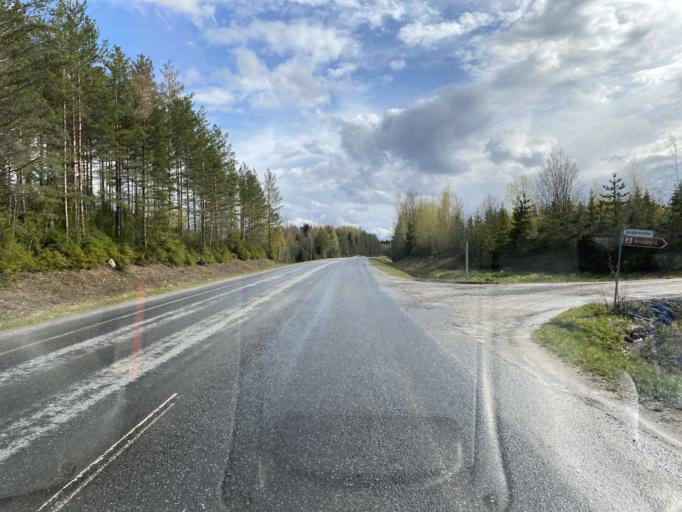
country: FI
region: Pirkanmaa
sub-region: Etelae-Pirkanmaa
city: Viiala
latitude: 61.1990
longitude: 23.7324
